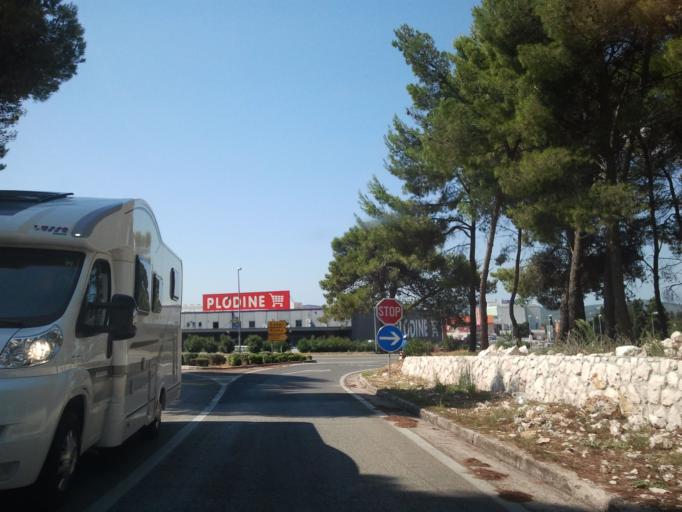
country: HR
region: Zadarska
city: Biograd na Moru
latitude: 43.9434
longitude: 15.4567
